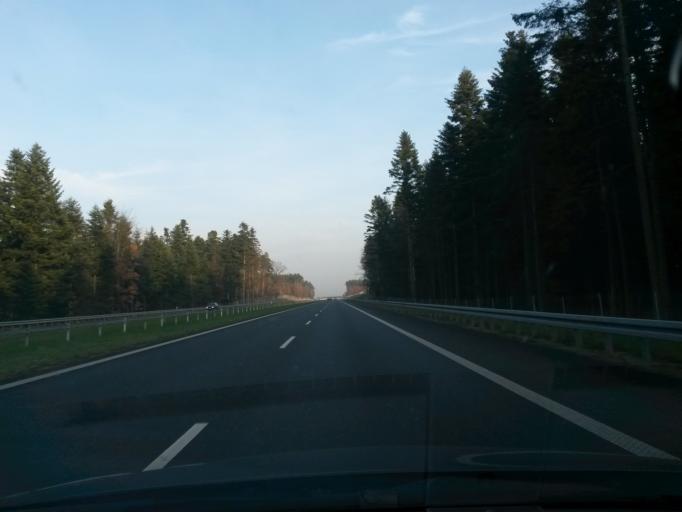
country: PL
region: Lodz Voivodeship
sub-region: Powiat wieruszowski
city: Galewice
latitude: 51.3185
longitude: 18.2851
